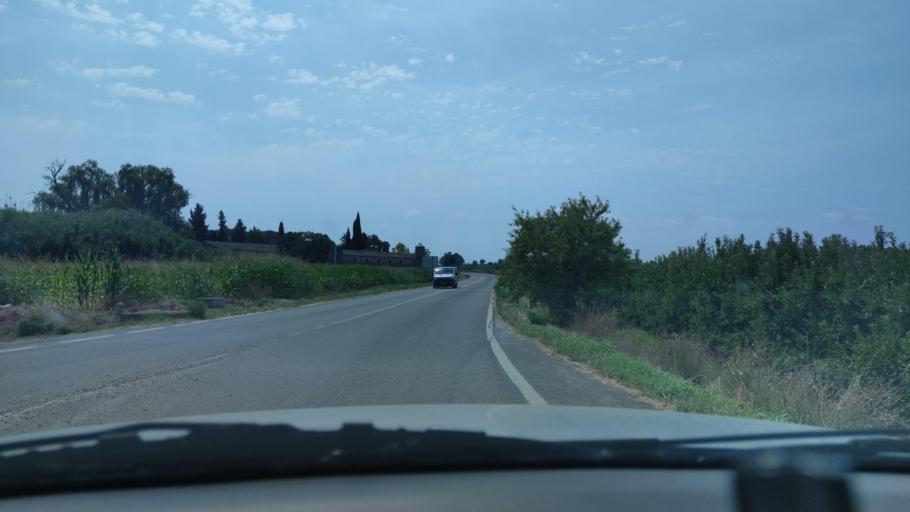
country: ES
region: Catalonia
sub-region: Provincia de Lleida
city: Bellpuig
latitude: 41.6185
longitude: 1.0208
